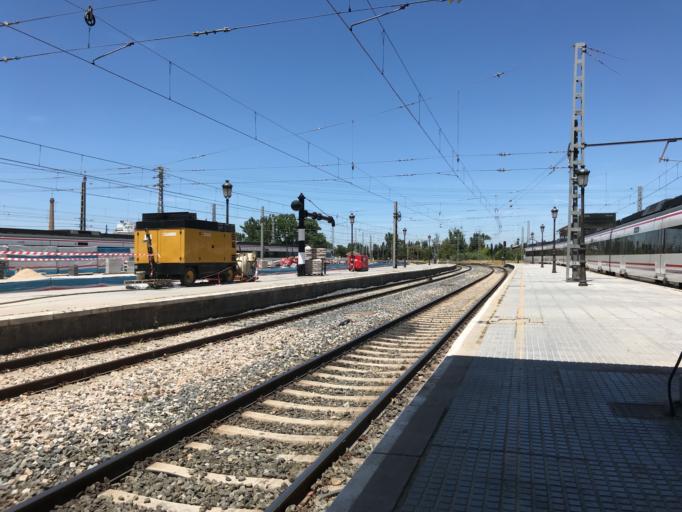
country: ES
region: Madrid
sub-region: Provincia de Madrid
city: Aranjuez
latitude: 40.0354
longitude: -3.6186
